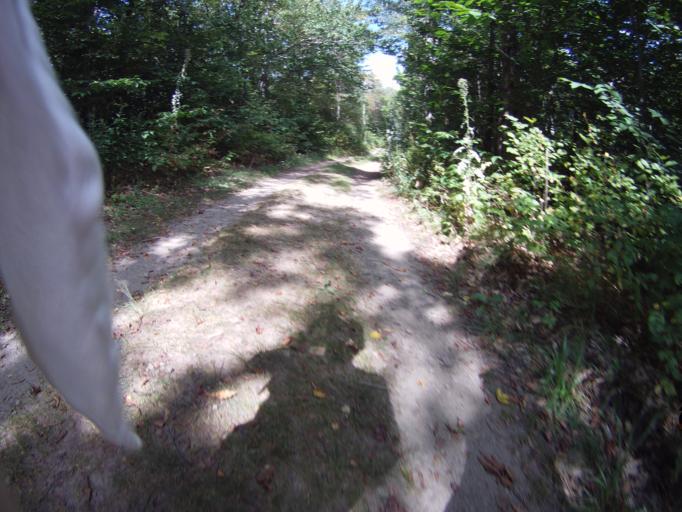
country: US
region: New York
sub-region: Ulster County
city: Woodstock
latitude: 42.1956
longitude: -74.2344
